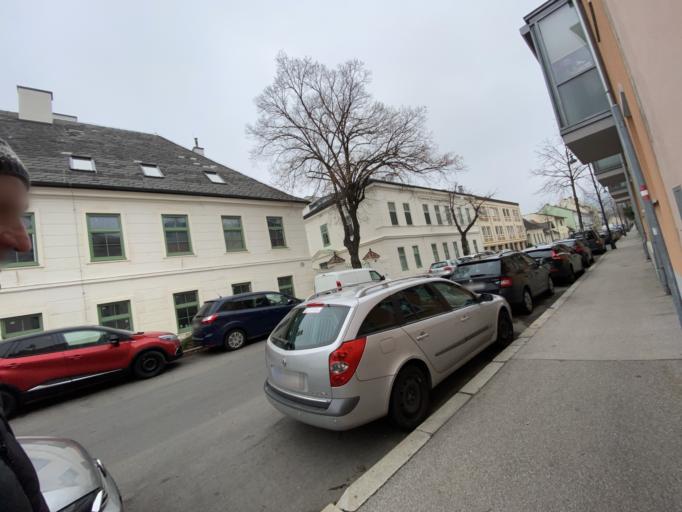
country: AT
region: Lower Austria
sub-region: Politischer Bezirk Baden
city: Baden
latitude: 48.0038
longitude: 16.2346
